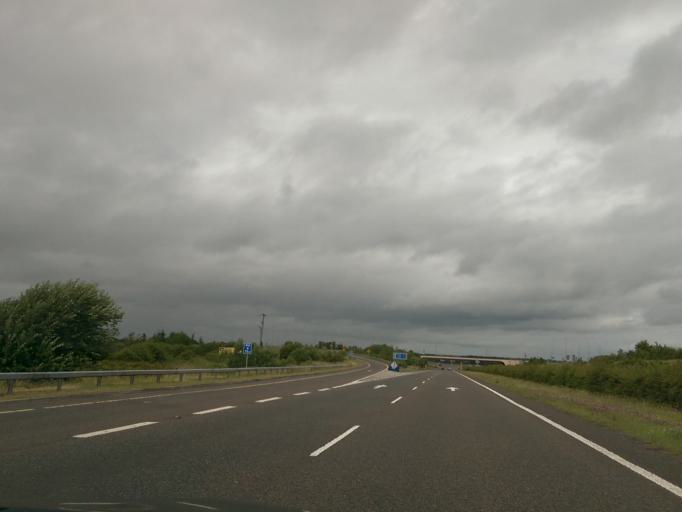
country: IE
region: Munster
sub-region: An Clar
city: Newmarket on Fergus
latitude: 52.7858
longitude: -8.9215
